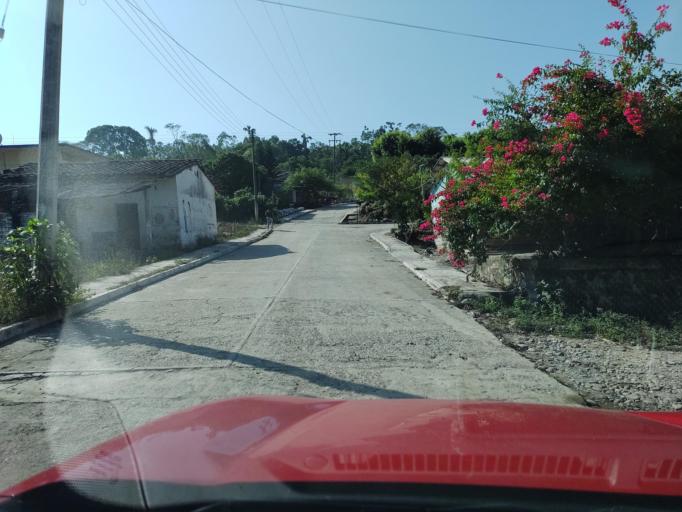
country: MX
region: Veracruz
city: Agua Dulce
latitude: 20.2889
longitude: -97.1828
